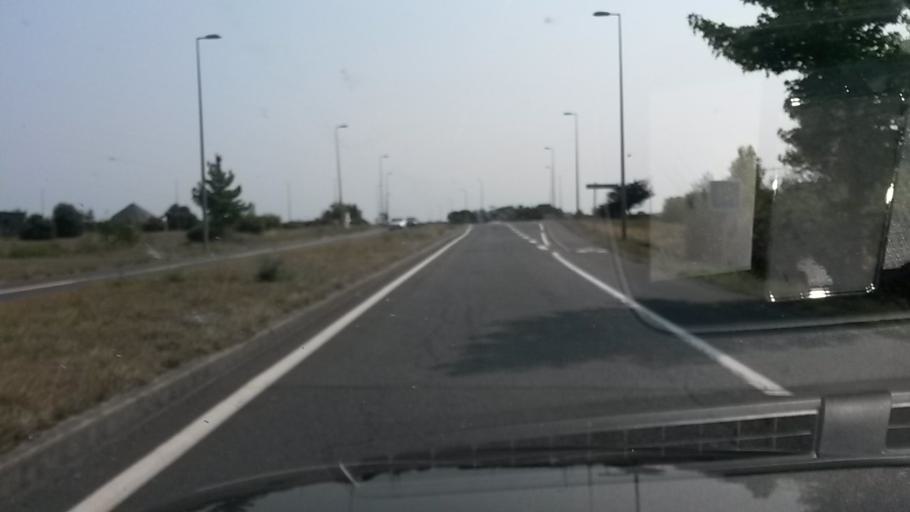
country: FR
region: Pays de la Loire
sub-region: Departement de la Loire-Atlantique
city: Saint-Gereon
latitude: 47.3961
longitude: -1.1899
